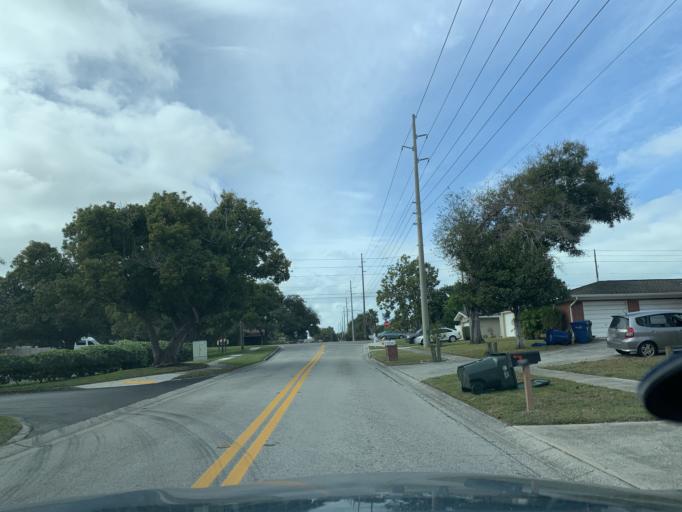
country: US
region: Florida
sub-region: Pinellas County
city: Ridgecrest
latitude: 27.8874
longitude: -82.7943
